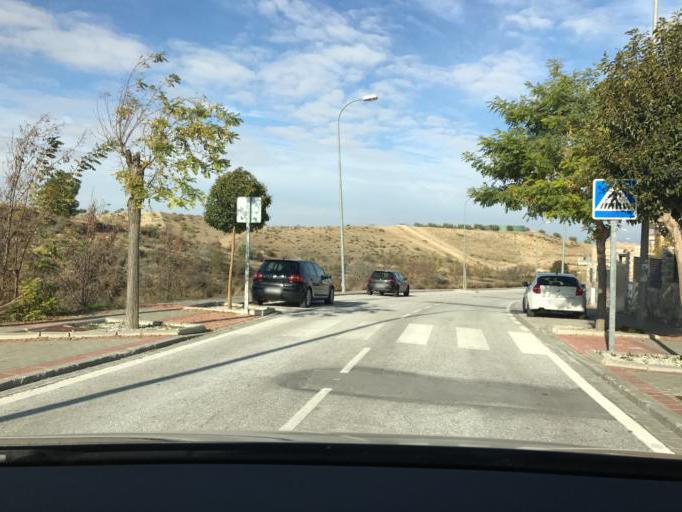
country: ES
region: Andalusia
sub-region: Provincia de Granada
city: Otura
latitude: 37.0722
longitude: -3.6373
